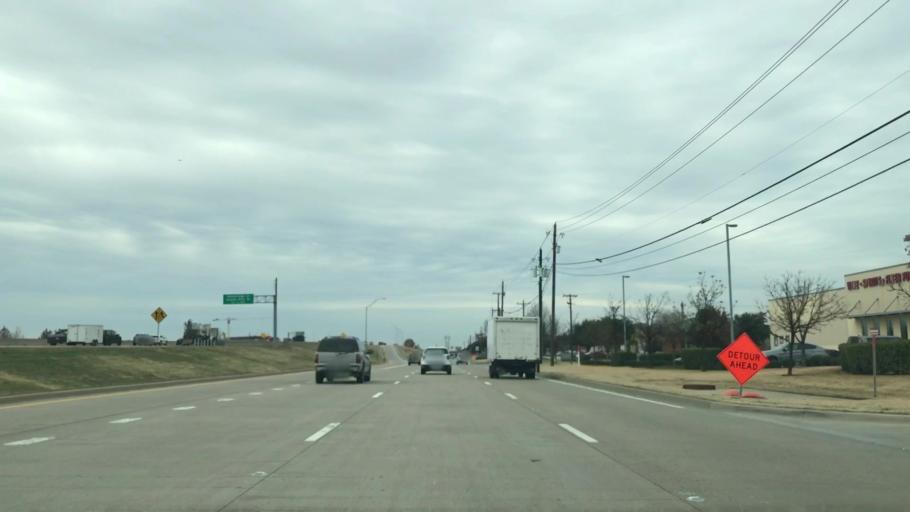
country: US
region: Texas
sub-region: Denton County
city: The Colony
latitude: 33.0690
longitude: -96.8830
